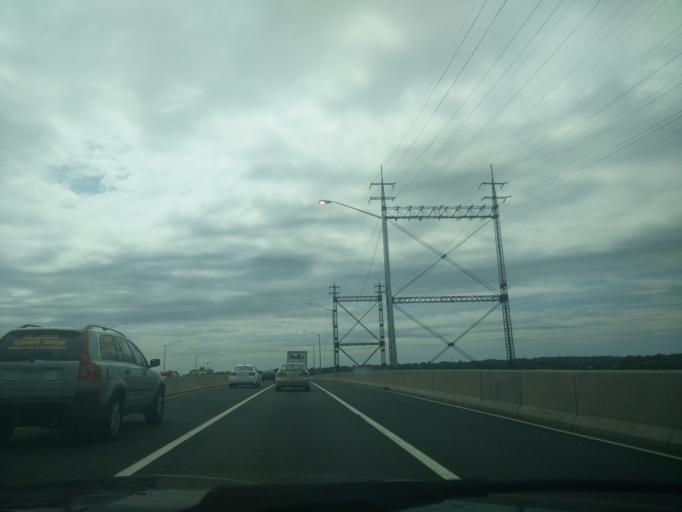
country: US
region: Connecticut
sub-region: Fairfield County
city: Stratford
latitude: 41.2053
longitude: -73.1087
